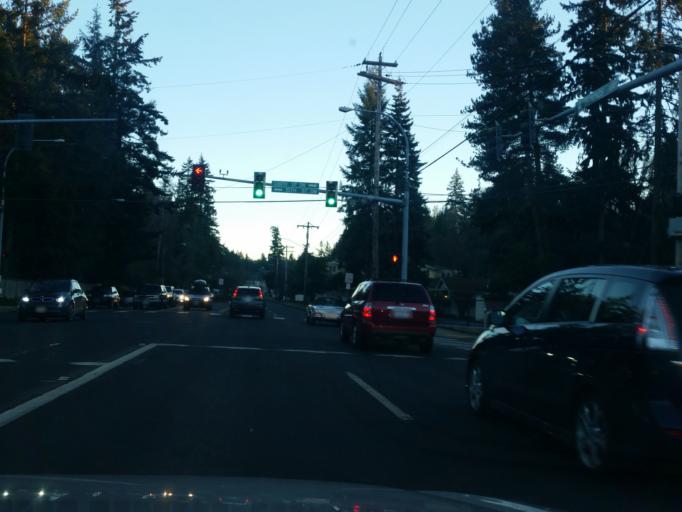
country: US
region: Washington
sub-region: Snohomish County
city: Woodway
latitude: 47.7943
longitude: -122.3723
